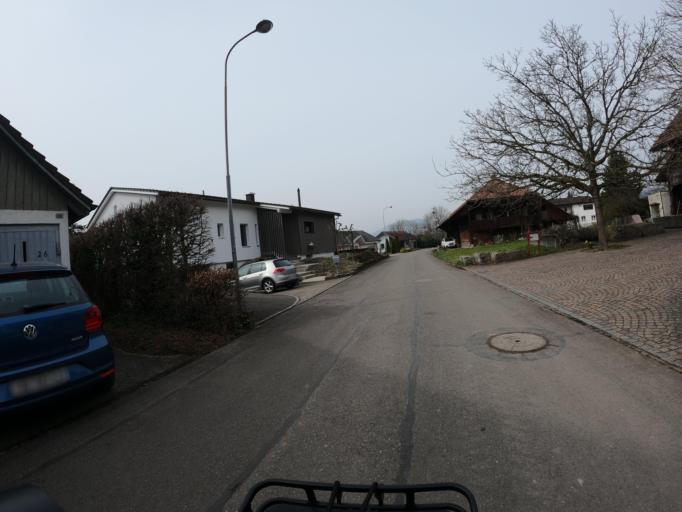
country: CH
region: Aargau
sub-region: Bezirk Lenzburg
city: Niederlenz
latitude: 47.4123
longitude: 8.1840
